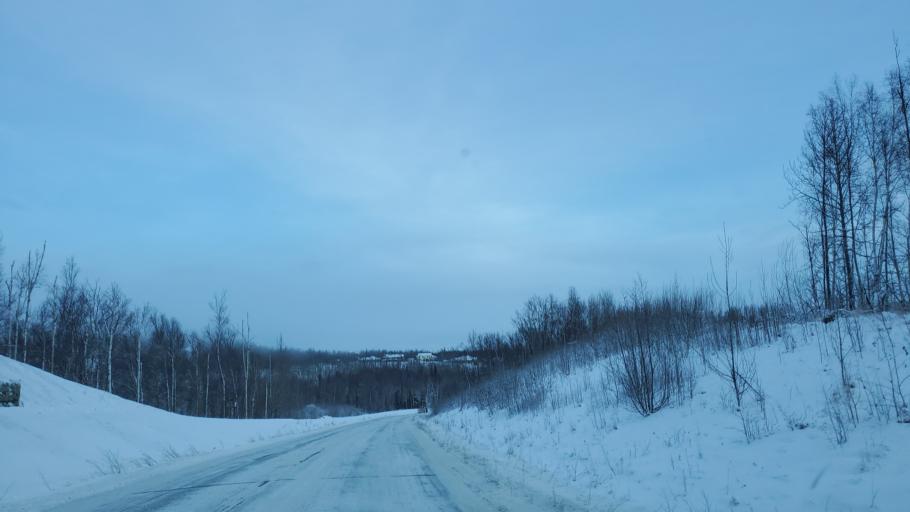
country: US
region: Alaska
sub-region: Matanuska-Susitna Borough
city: Lakes
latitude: 61.5499
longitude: -149.3045
